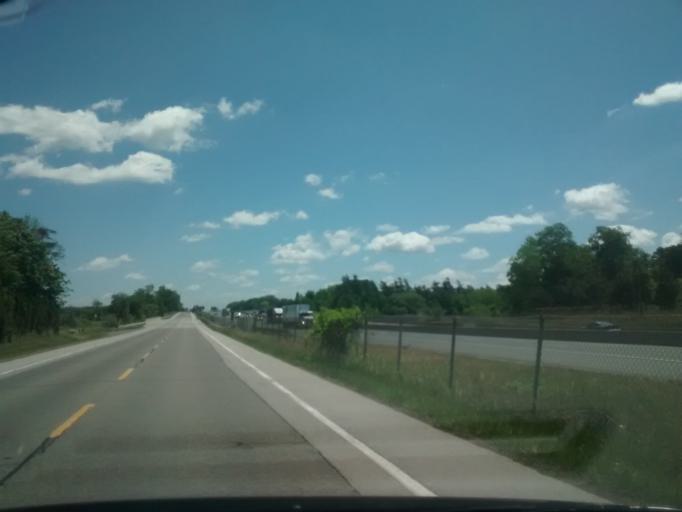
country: CA
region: Ontario
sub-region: Regional Municipality of Niagara
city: St. Catharines
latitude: 43.1799
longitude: -79.3415
